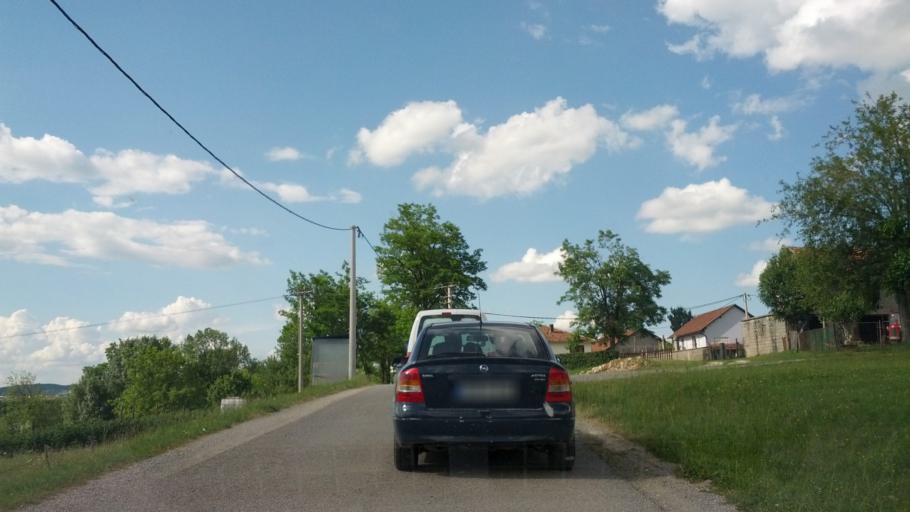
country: BA
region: Federation of Bosnia and Herzegovina
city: Ostrozac
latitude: 44.9274
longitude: 15.9559
